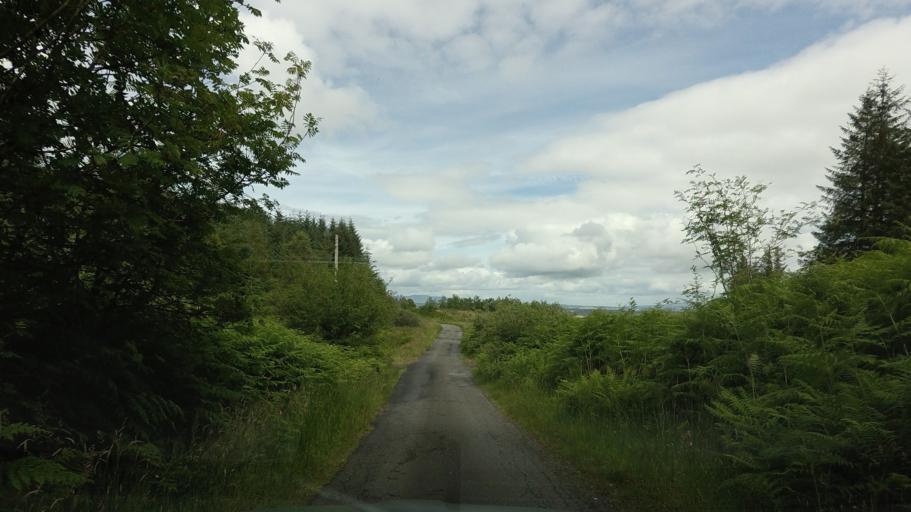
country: GB
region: Scotland
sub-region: Stirling
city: Killearn
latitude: 56.1096
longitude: -4.4075
